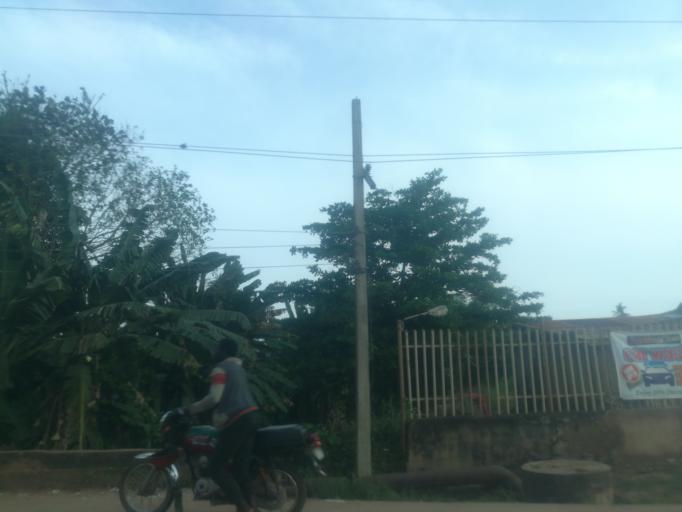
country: NG
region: Ogun
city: Abeokuta
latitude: 7.1321
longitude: 3.3292
